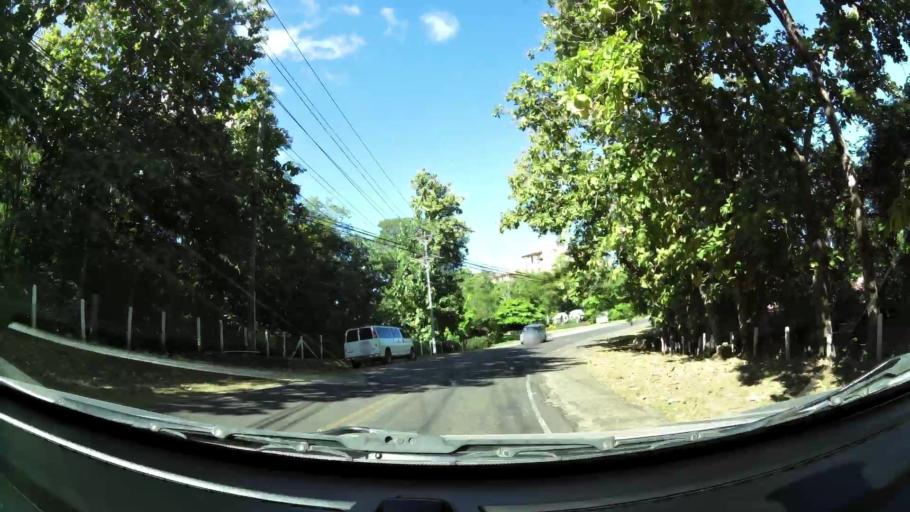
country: CR
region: Guanacaste
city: Sardinal
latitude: 10.3985
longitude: -85.7940
